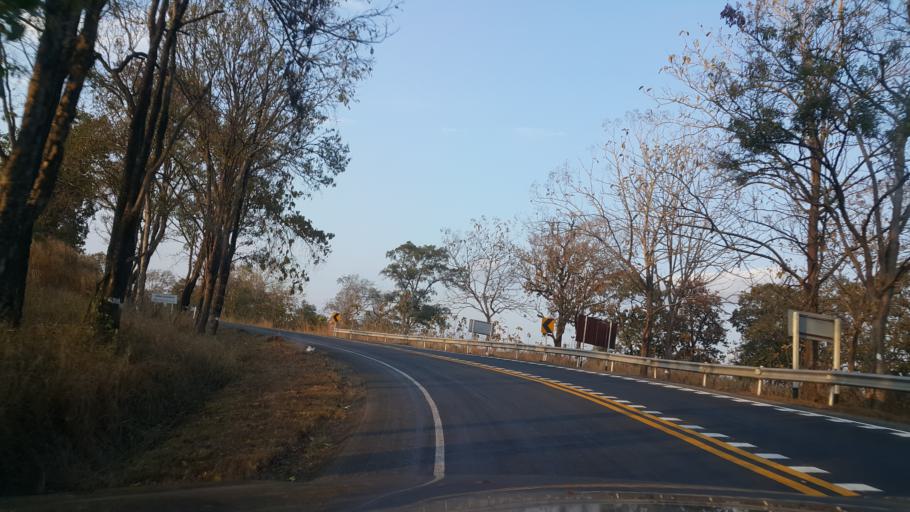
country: TH
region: Loei
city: Phu Ruea
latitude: 17.4674
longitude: 101.5345
